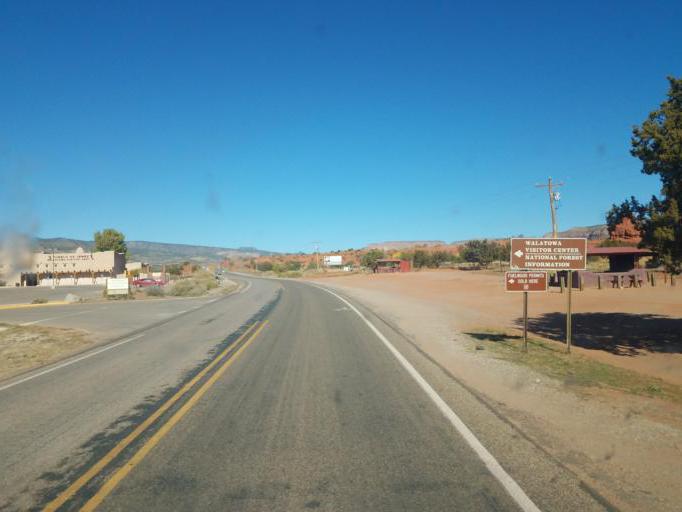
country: US
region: New Mexico
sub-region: Sandoval County
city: Jemez Pueblo
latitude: 35.6443
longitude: -106.7251
